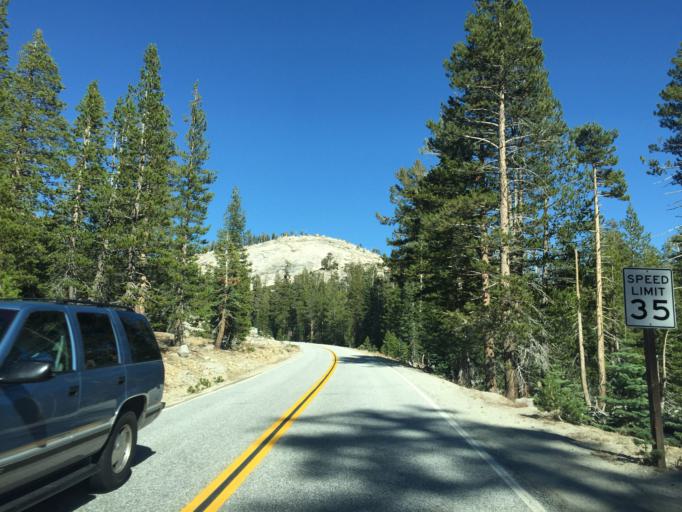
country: US
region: California
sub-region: Mariposa County
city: Yosemite Valley
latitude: 37.8157
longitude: -119.5201
